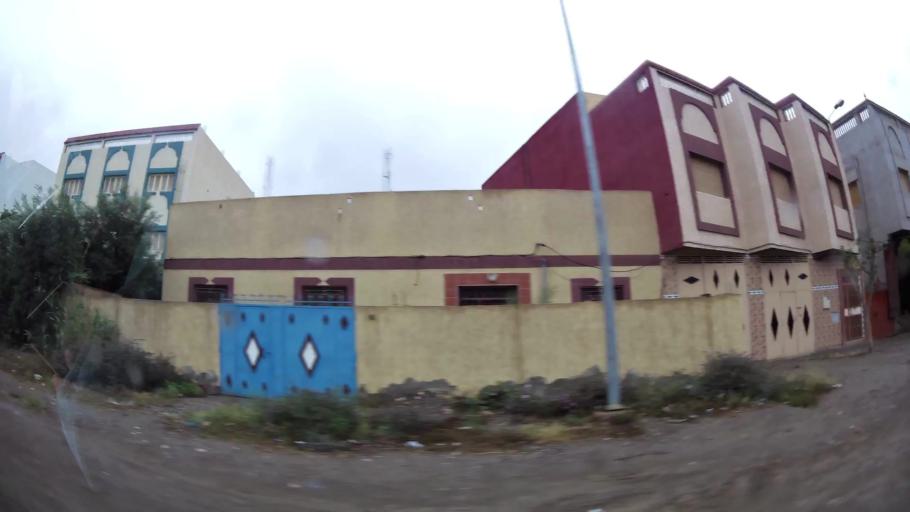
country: MA
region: Taza-Al Hoceima-Taounate
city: Imzourene
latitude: 35.1542
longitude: -3.8293
